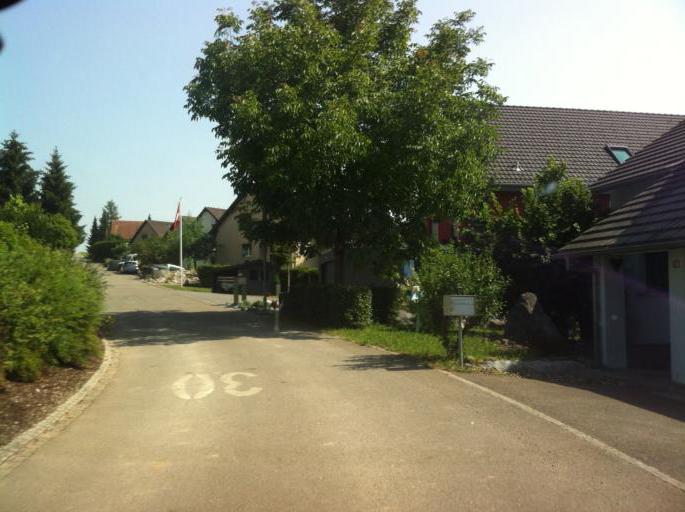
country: CH
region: Thurgau
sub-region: Frauenfeld District
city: Diessenhofen
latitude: 47.6670
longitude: 8.7485
